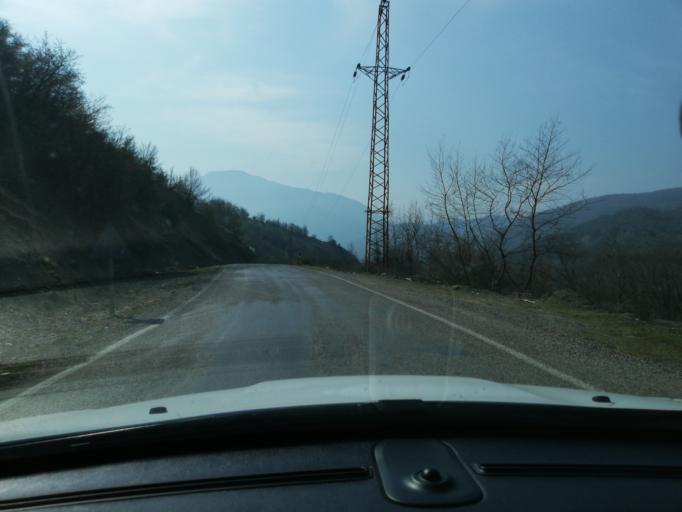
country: TR
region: Karabuk
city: Yenice
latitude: 41.2359
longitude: 32.3601
